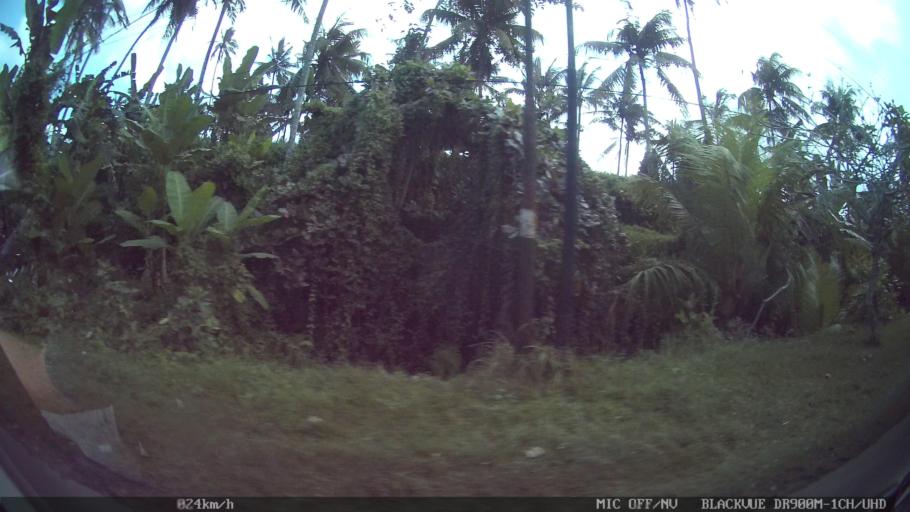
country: ID
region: Bali
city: Banjar Pesalakan
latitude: -8.4889
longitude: 115.2979
